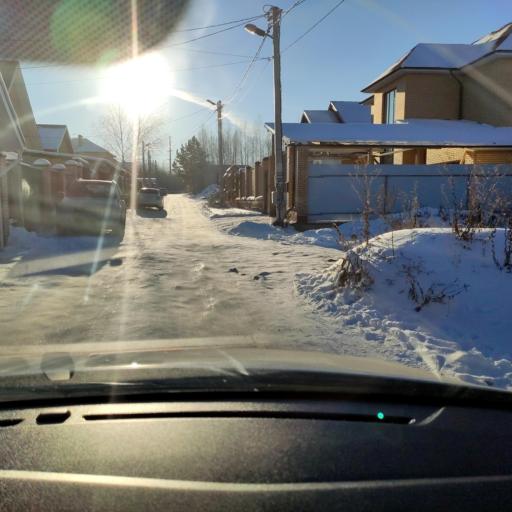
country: RU
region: Tatarstan
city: Stolbishchi
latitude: 55.7334
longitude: 49.2610
